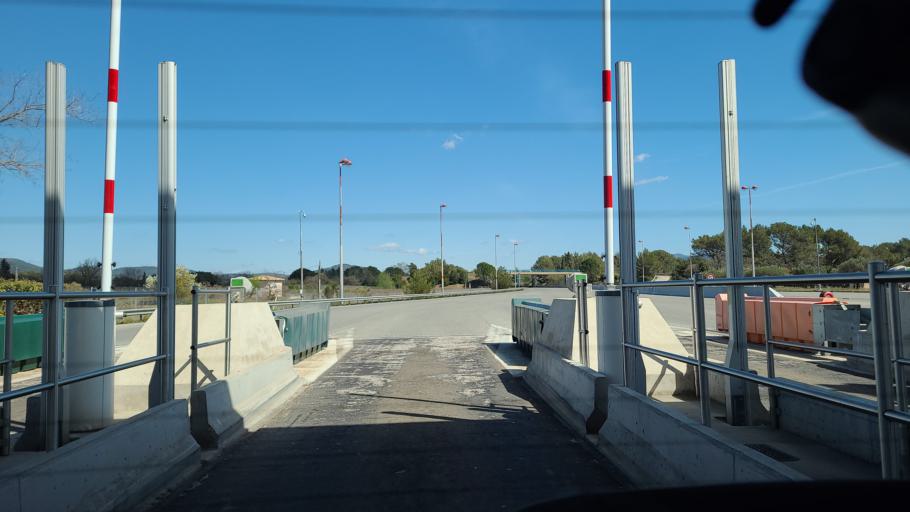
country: FR
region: Provence-Alpes-Cote d'Azur
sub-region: Departement du Var
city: Puget-Ville
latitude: 43.2580
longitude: 6.1227
